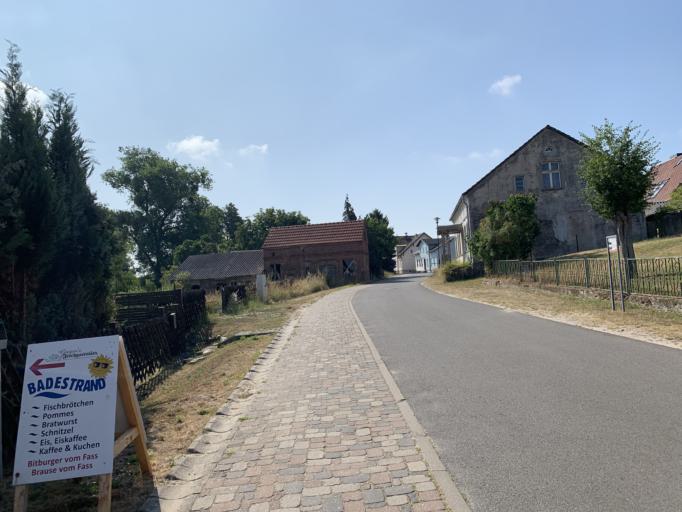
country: PL
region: West Pomeranian Voivodeship
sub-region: Powiat policki
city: Nowe Warpno
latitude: 53.7420
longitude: 14.2659
